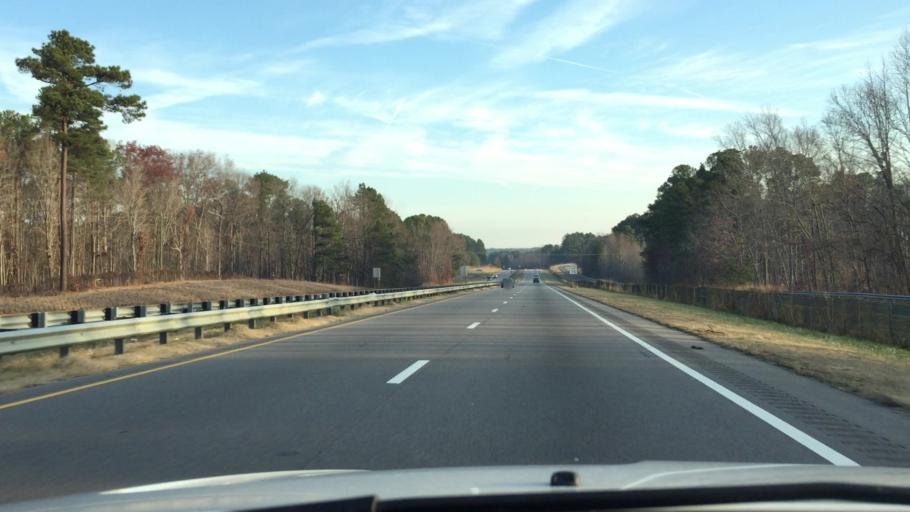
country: US
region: North Carolina
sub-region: Lee County
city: Sanford
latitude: 35.4541
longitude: -79.2121
